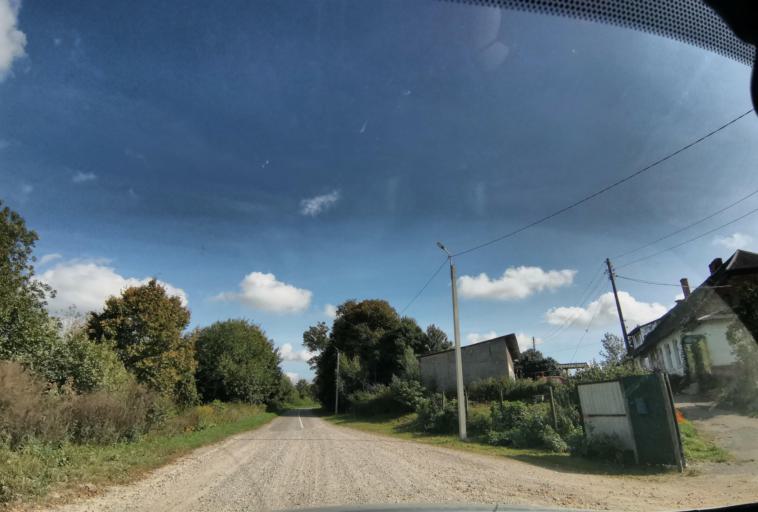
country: RU
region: Kaliningrad
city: Gusev
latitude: 54.6505
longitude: 22.0520
